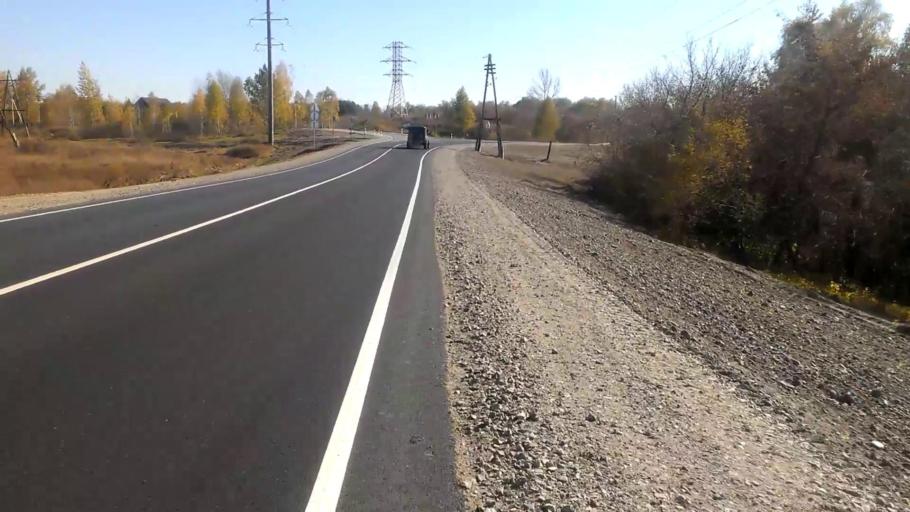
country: RU
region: Altai Krai
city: Sannikovo
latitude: 53.3286
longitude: 83.9400
